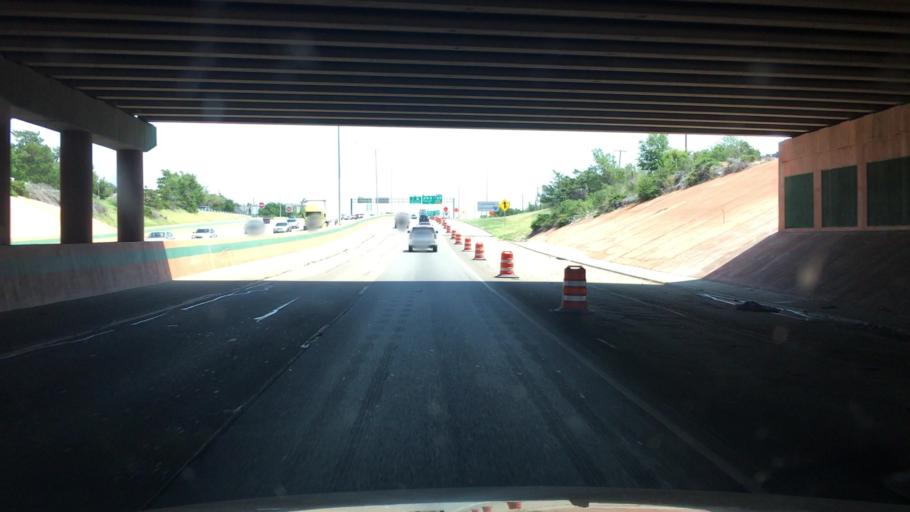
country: US
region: Texas
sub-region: Potter County
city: Amarillo
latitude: 35.1944
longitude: -101.8487
